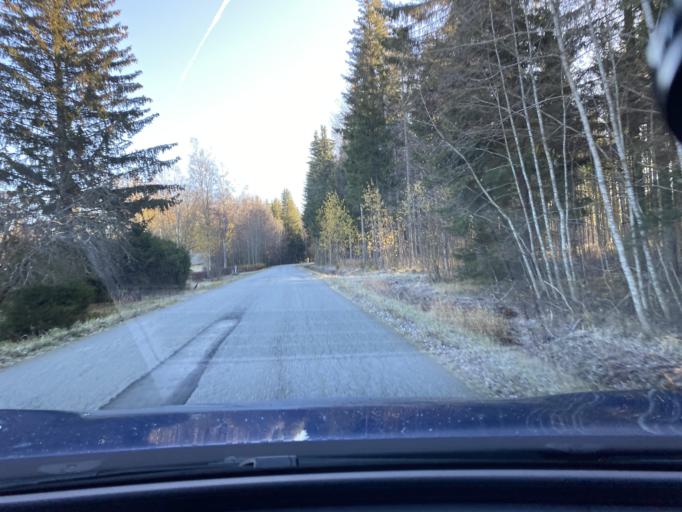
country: FI
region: Pirkanmaa
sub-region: Etelae-Pirkanmaa
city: Kylmaekoski
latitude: 61.0468
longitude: 23.7402
